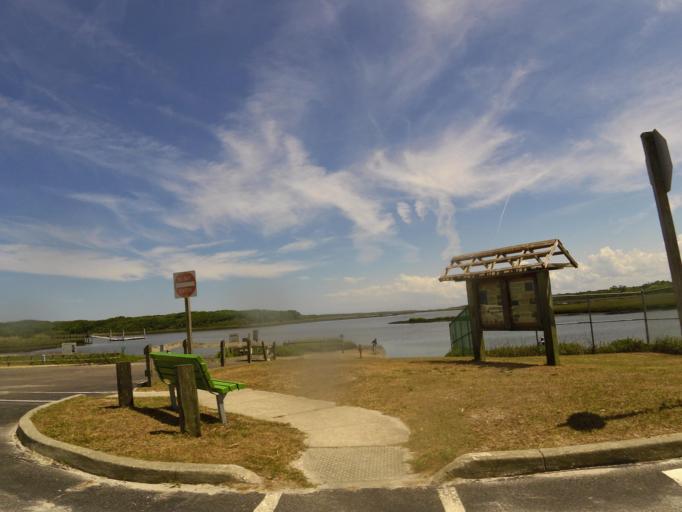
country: US
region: Florida
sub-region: Saint Johns County
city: Villano Beach
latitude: 30.0230
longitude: -81.3281
